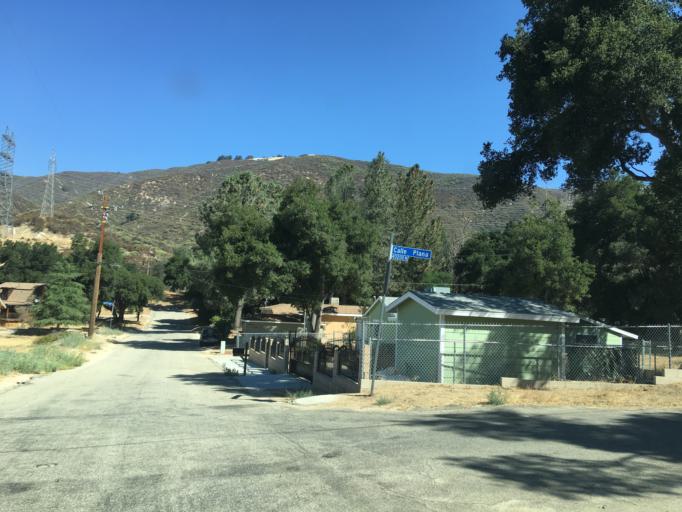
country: US
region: California
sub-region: Los Angeles County
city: Green Valley
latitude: 34.6258
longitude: -118.4061
